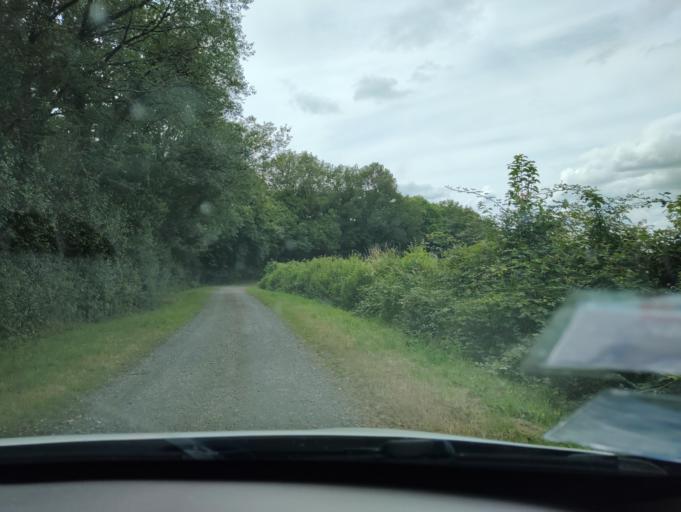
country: FR
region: Pays de la Loire
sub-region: Departement de la Loire-Atlantique
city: Chateaubriant
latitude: 47.7011
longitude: -1.4187
